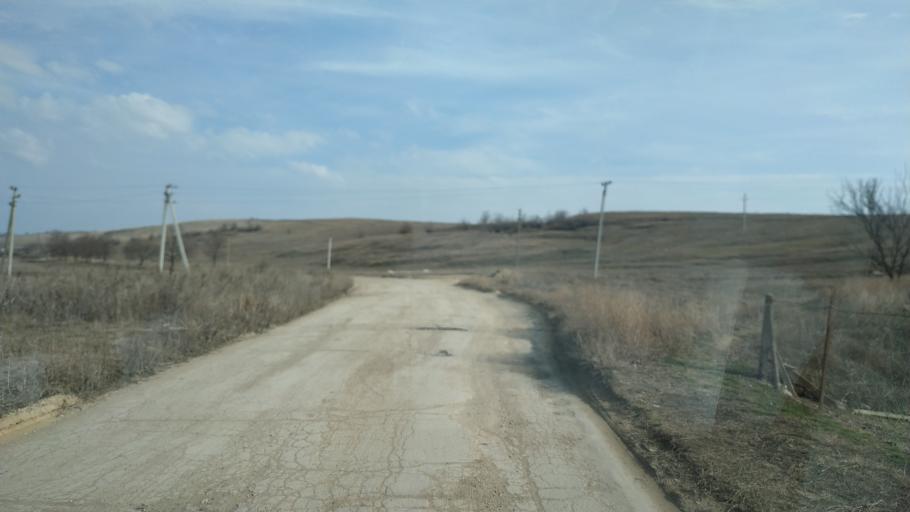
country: MD
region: Chisinau
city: Singera
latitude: 46.9292
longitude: 29.1042
